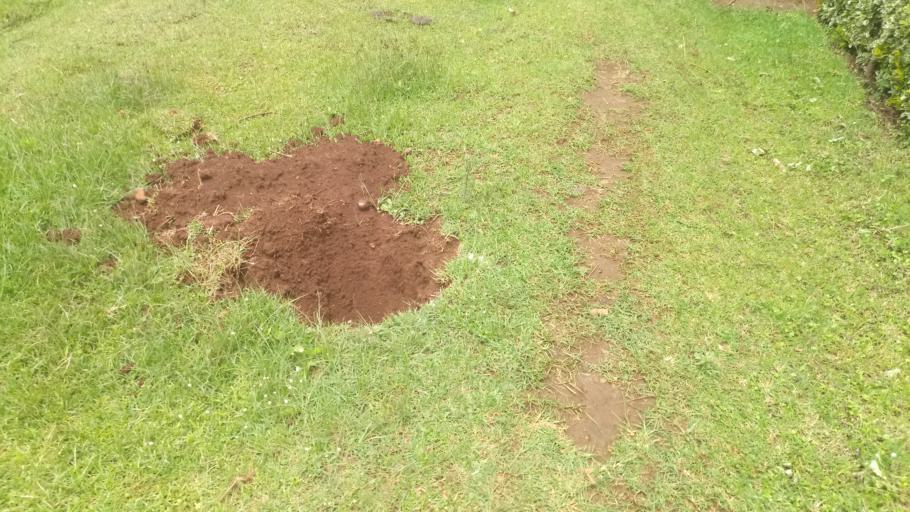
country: KE
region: Kirinyaga
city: Keruguya
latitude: -0.4033
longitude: 37.1560
